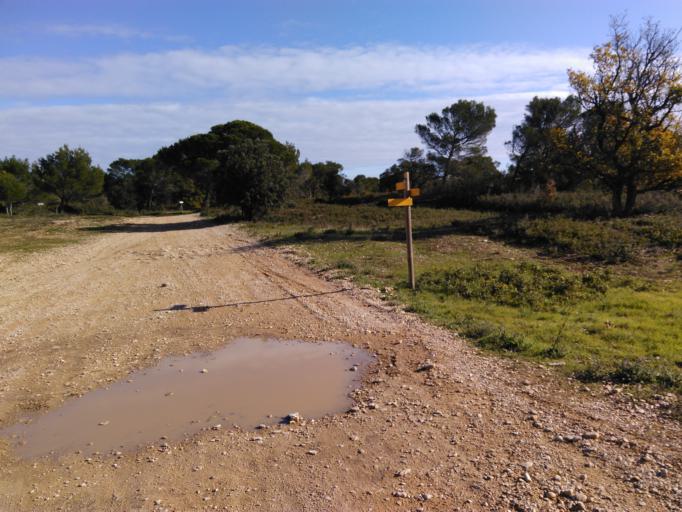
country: FR
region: Provence-Alpes-Cote d'Azur
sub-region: Departement du Vaucluse
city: Piolenc
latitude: 44.2089
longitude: 4.7586
